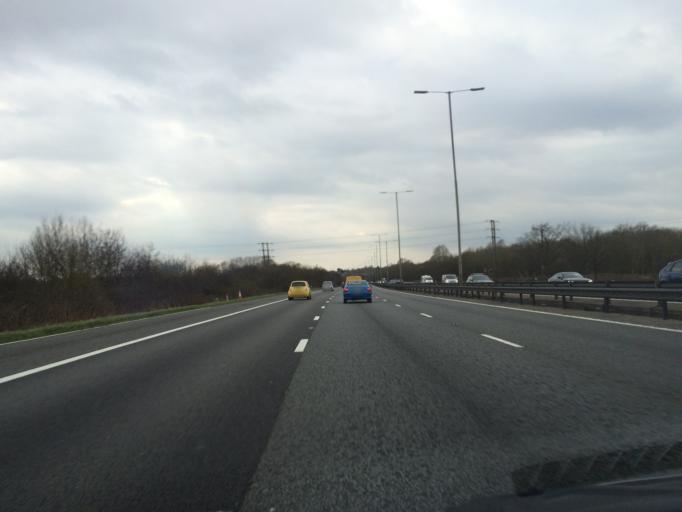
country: GB
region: England
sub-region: Wokingham
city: Lower Earley
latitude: 51.4199
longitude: -0.9167
